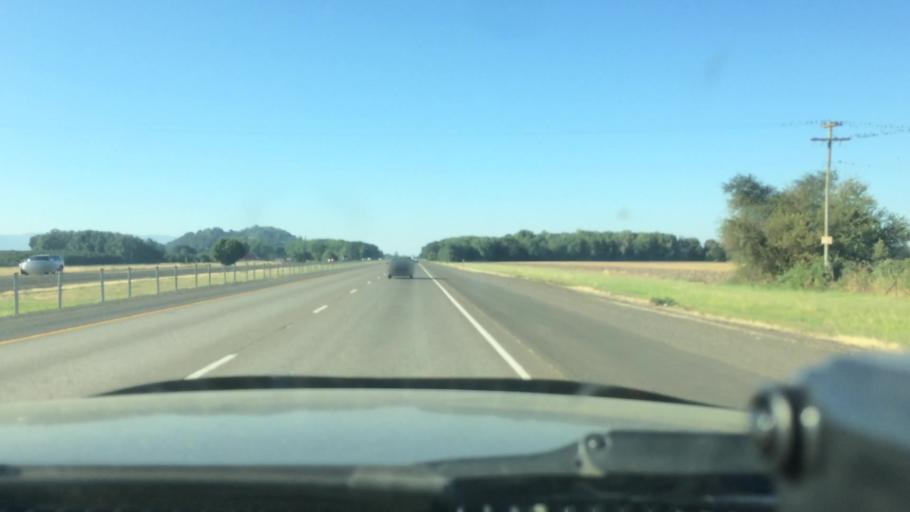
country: US
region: Oregon
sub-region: Linn County
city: Tangent
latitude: 44.4832
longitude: -123.0628
